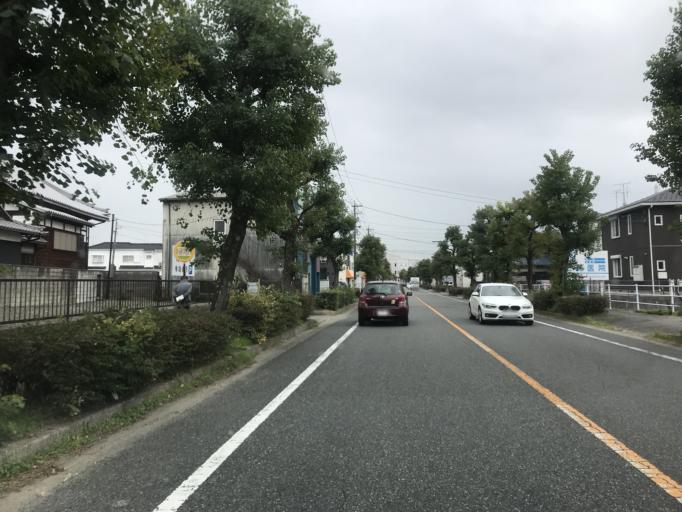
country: JP
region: Aichi
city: Nagoya-shi
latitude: 35.2038
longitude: 136.8397
